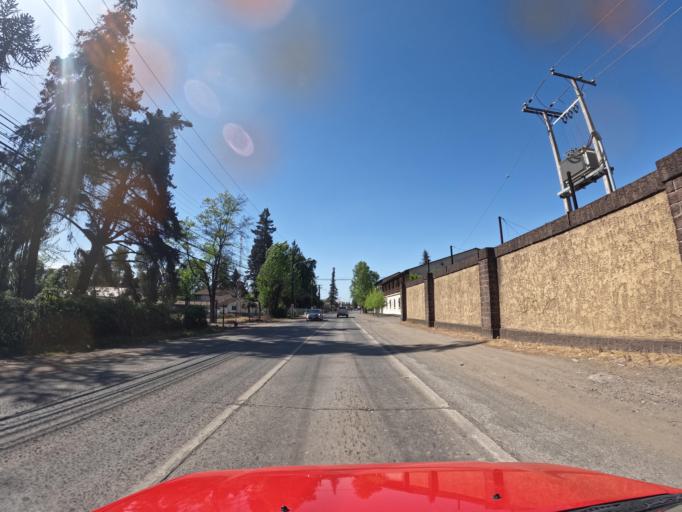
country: CL
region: Maule
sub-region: Provincia de Curico
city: Molina
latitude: -35.0787
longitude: -71.2607
